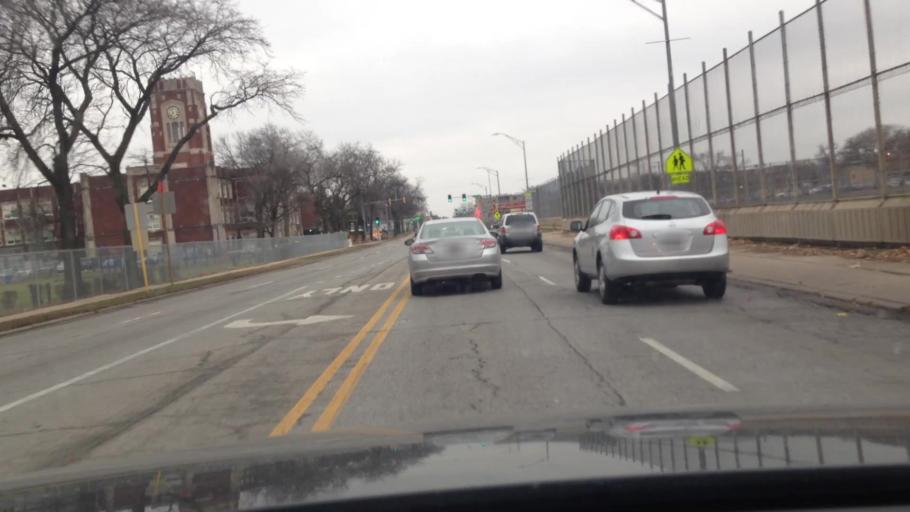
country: US
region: Illinois
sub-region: Cook County
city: Maywood
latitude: 41.8824
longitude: -87.8342
